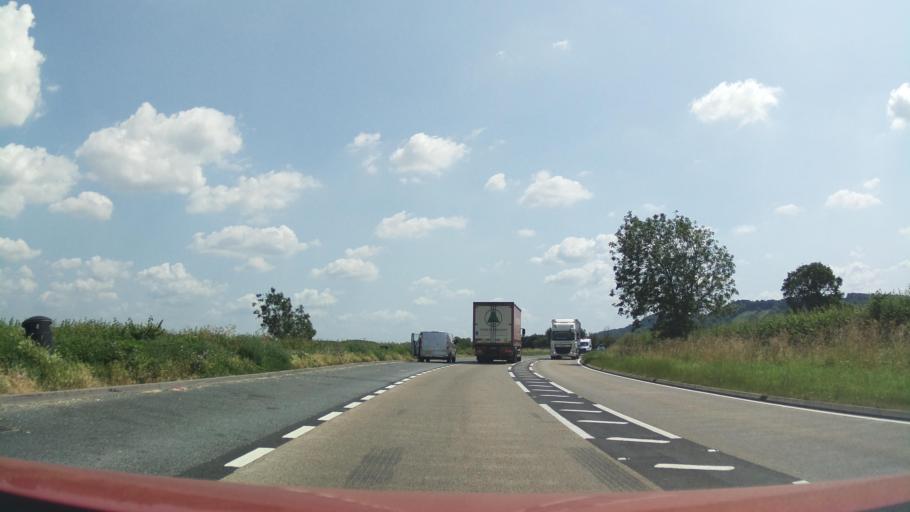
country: GB
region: England
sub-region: Gloucestershire
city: Gotherington
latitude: 52.0030
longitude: -2.0794
